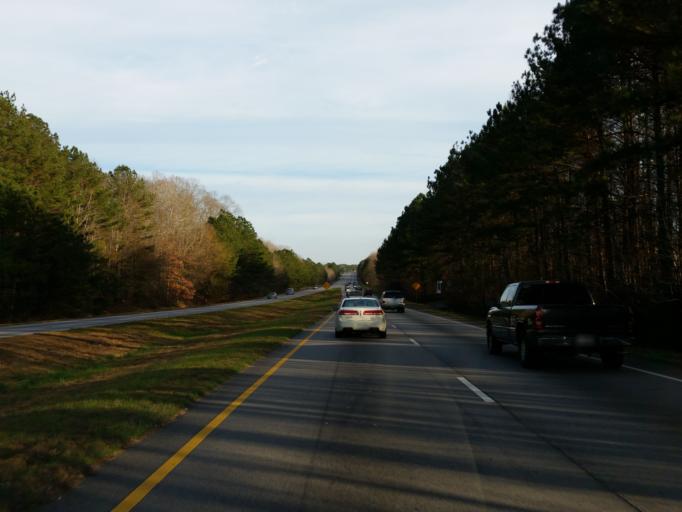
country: US
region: Georgia
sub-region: Cobb County
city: Powder Springs
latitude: 33.8790
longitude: -84.7163
